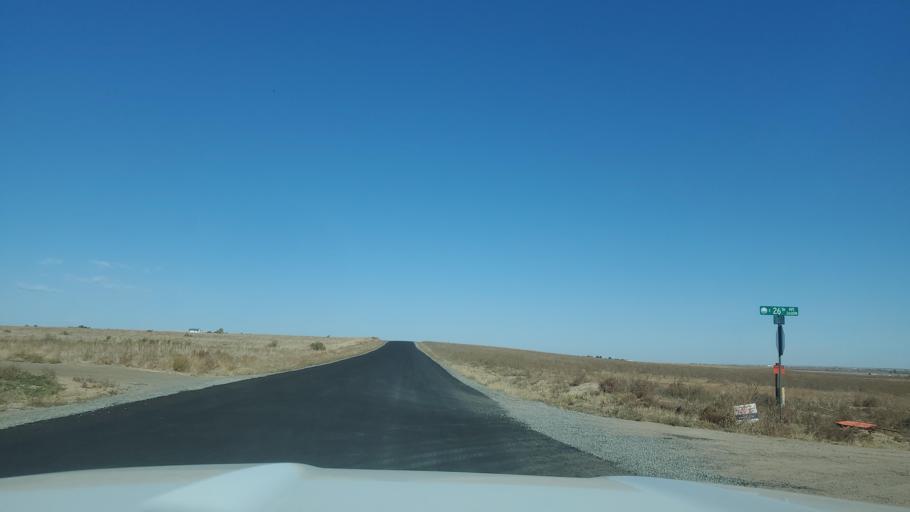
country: US
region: Colorado
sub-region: Adams County
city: Bennett
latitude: 39.7525
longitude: -104.3771
